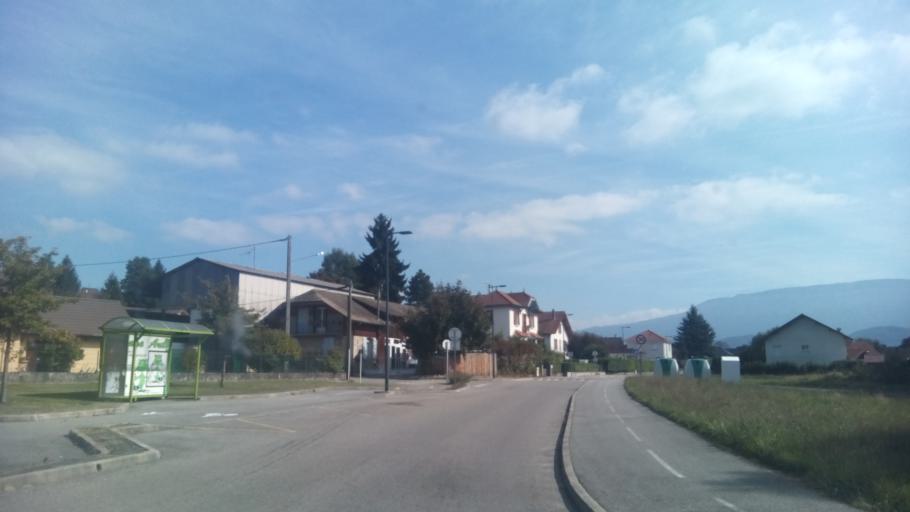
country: FR
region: Rhone-Alpes
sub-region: Departement de la Savoie
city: Le Pont-de-Beauvoisin
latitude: 45.5364
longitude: 5.6828
